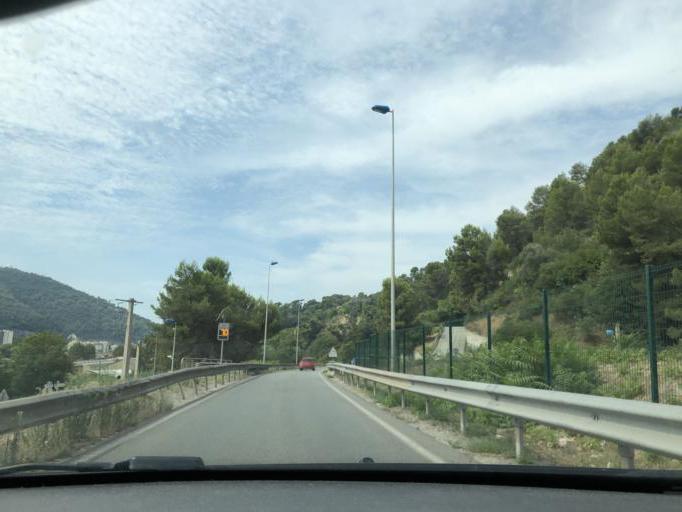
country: FR
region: Provence-Alpes-Cote d'Azur
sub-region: Departement des Alpes-Maritimes
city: La Trinite
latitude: 43.7470
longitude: 7.3153
